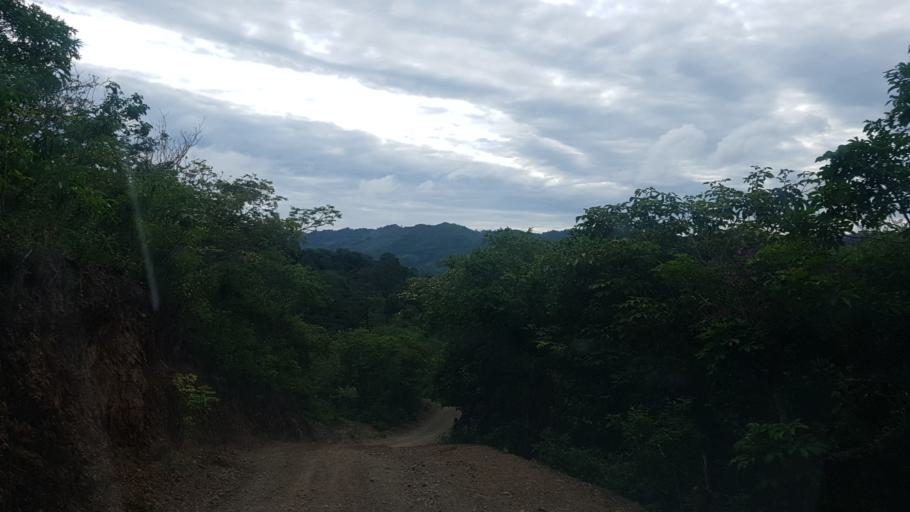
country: NI
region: Nueva Segovia
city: Ocotal
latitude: 13.5966
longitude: -86.4204
